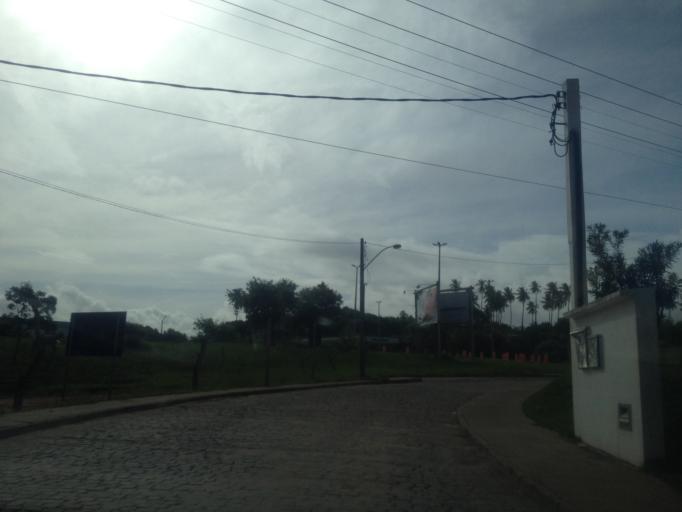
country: BR
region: Bahia
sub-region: Mata De Sao Joao
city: Mata de Sao Joao
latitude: -12.4939
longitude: -37.9696
